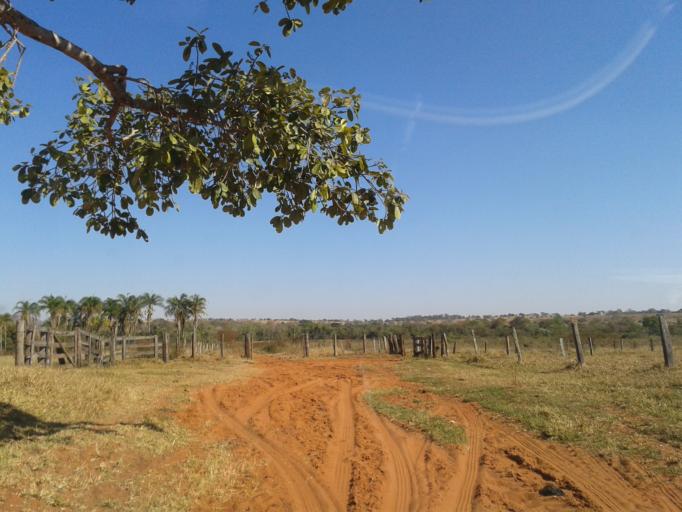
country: BR
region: Minas Gerais
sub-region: Santa Vitoria
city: Santa Vitoria
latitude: -19.0392
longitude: -49.9580
